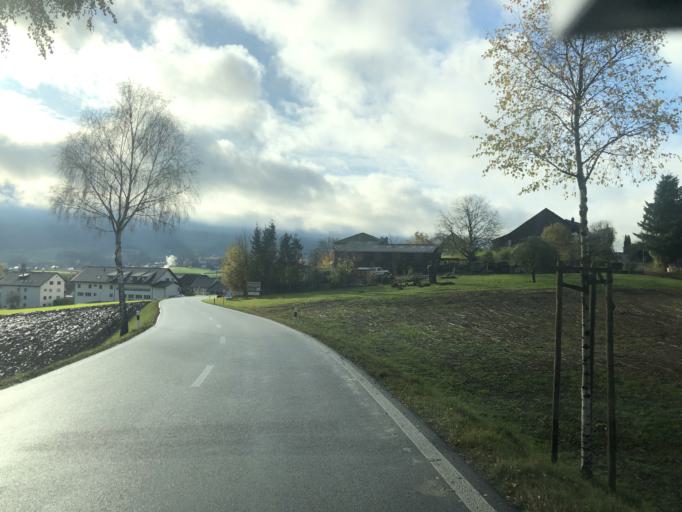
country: CH
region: Aargau
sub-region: Bezirk Baden
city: Unterehrendingen
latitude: 47.5206
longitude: 8.3662
